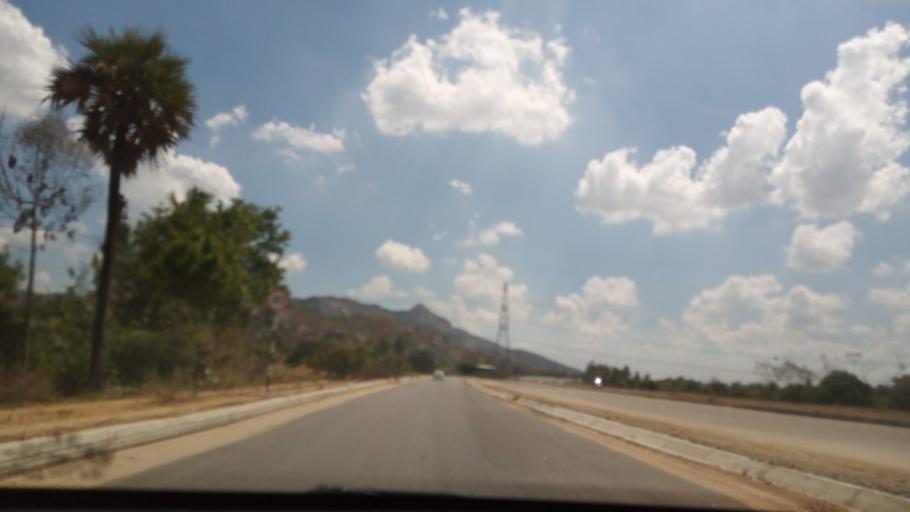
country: IN
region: Andhra Pradesh
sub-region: Chittoor
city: Pakala
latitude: 13.3431
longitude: 79.0819
